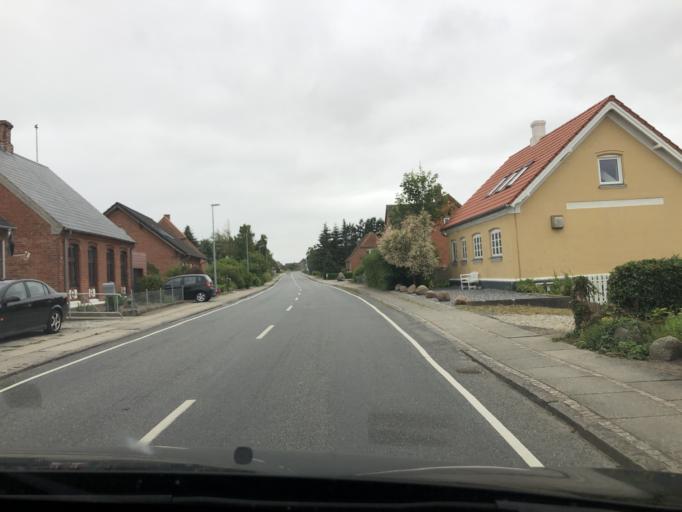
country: DK
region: South Denmark
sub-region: AEro Kommune
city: AEroskobing
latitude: 54.9369
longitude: 10.2598
